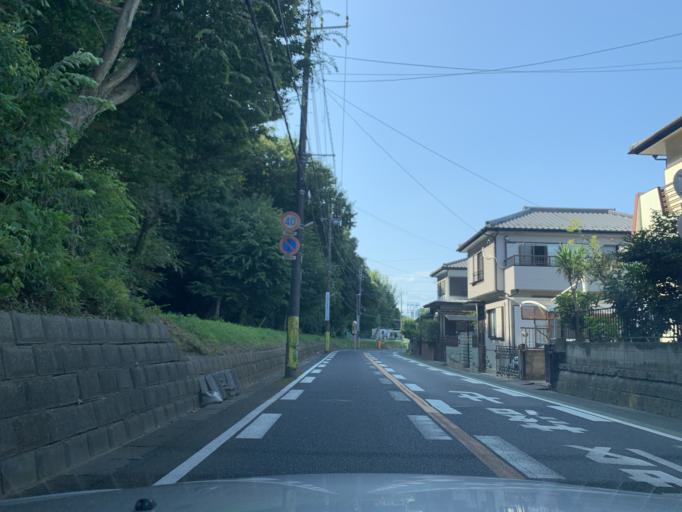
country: JP
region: Chiba
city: Nagareyama
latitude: 35.8446
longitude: 139.9351
